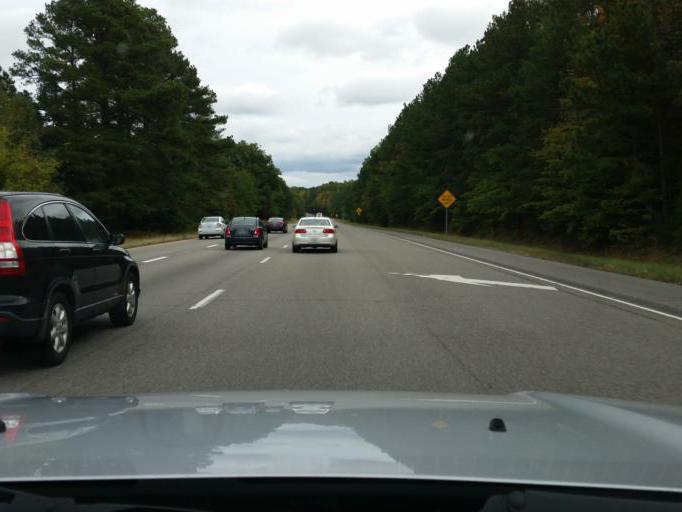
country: US
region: Virginia
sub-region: Henrico County
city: Sandston
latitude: 37.5162
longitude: -77.2536
